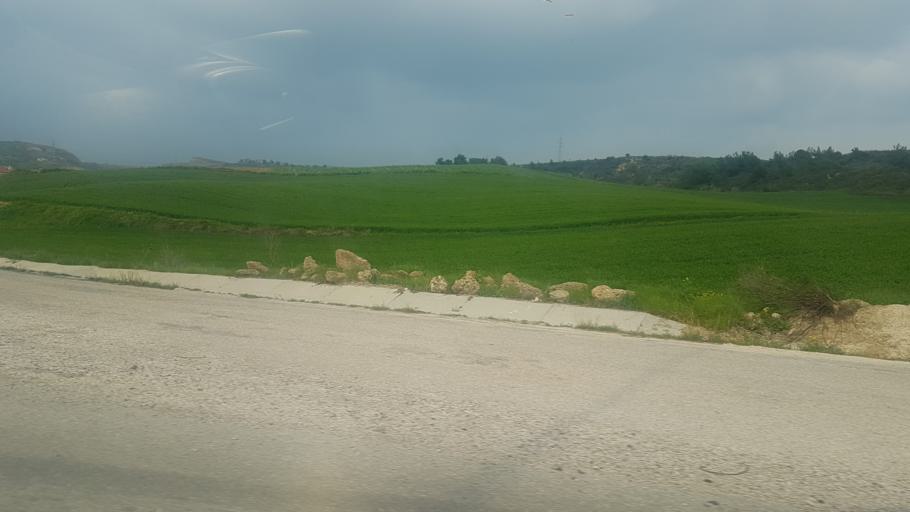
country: TR
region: Adana
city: Seyhan
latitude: 37.0470
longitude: 35.1794
